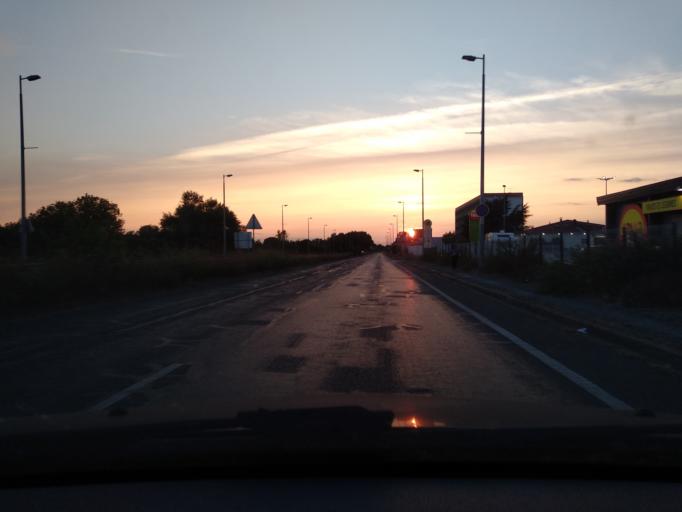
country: FR
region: Centre
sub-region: Departement d'Indre-et-Loire
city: La Riche
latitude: 47.3748
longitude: 0.6707
